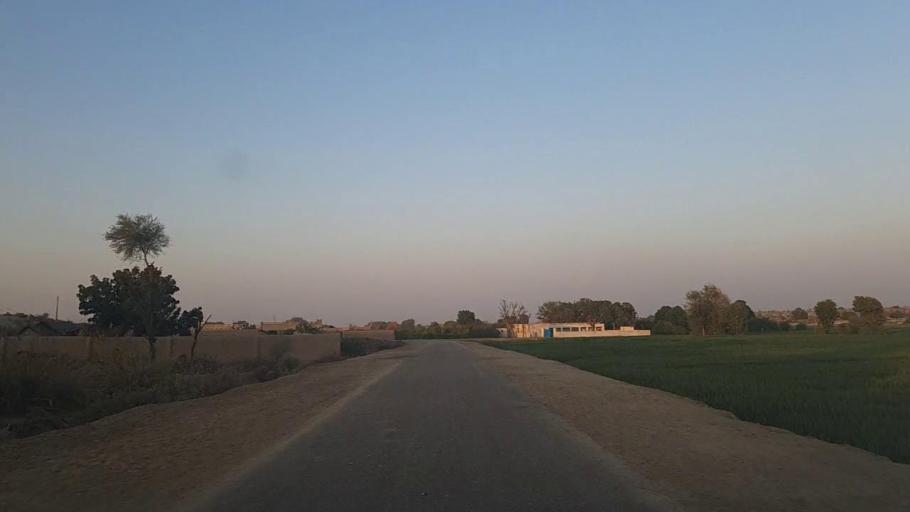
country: PK
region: Sindh
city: Jam Sahib
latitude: 26.3700
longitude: 68.7226
